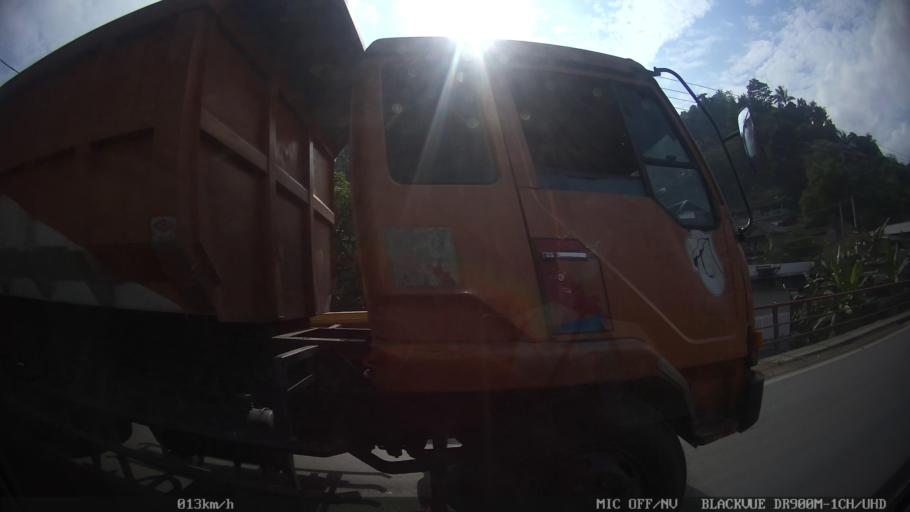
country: ID
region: Lampung
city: Panjang
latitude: -5.4740
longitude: 105.3251
